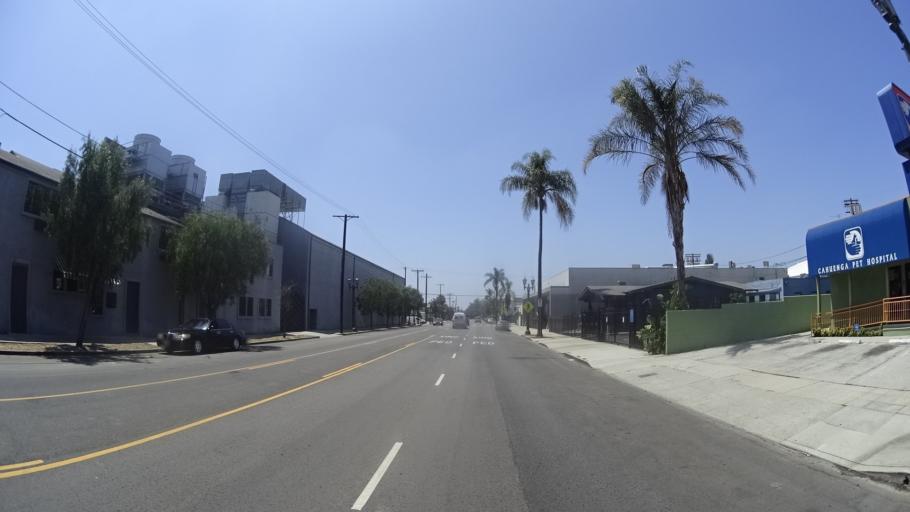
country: US
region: California
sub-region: Los Angeles County
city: Hollywood
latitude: 34.0863
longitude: -118.3289
